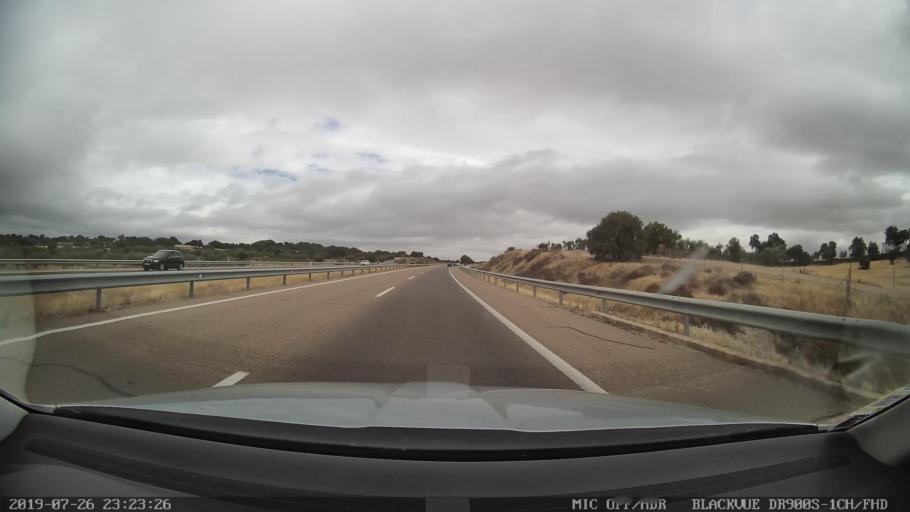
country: ES
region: Extremadura
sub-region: Provincia de Caceres
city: Miajadas
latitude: 39.1609
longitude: -5.9221
